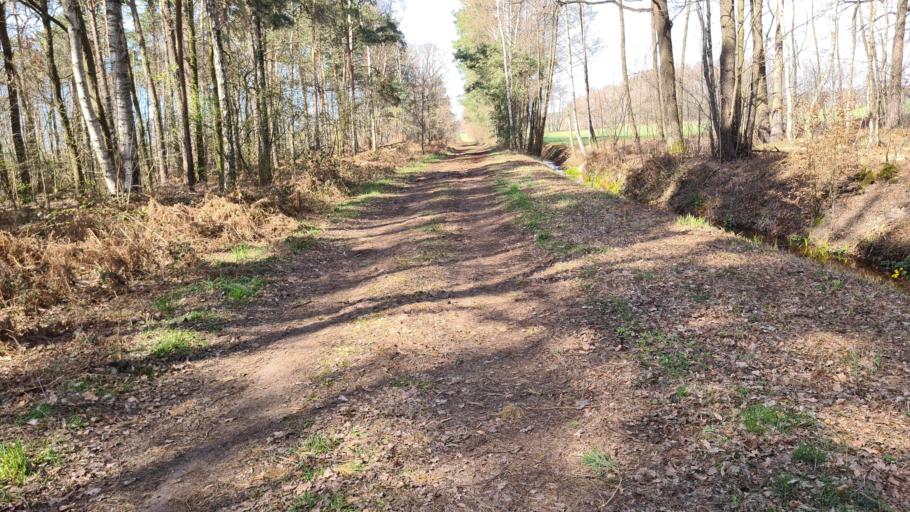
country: DE
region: Brandenburg
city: Finsterwalde
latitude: 51.6000
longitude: 13.6433
